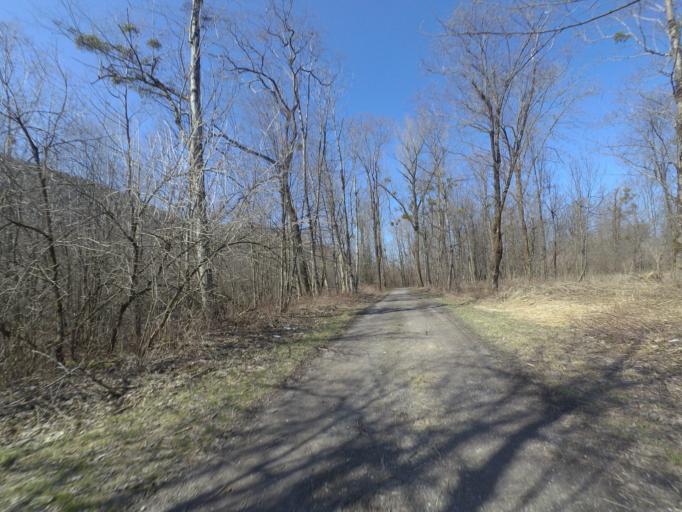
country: AT
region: Salzburg
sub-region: Politischer Bezirk Hallein
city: Kuchl
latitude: 47.6374
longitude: 13.1310
